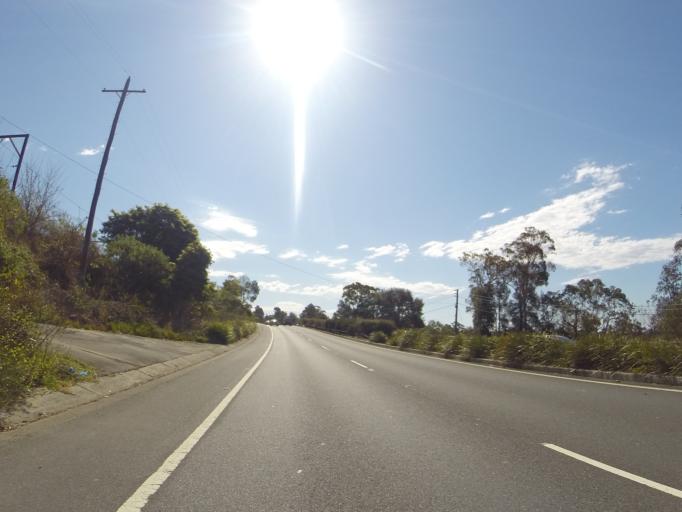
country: AU
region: New South Wales
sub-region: Blue Mountains Municipality
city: Blaxland
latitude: -33.7079
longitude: 150.5858
